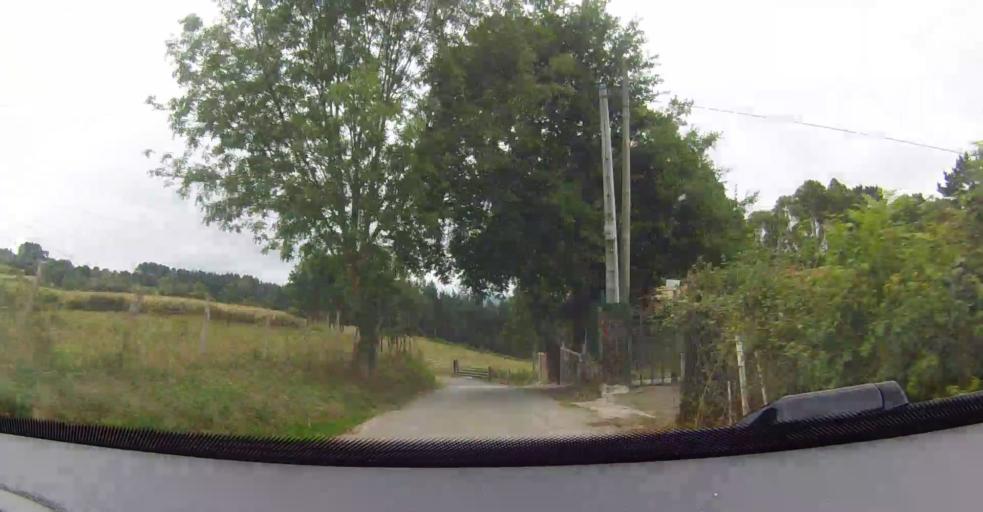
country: ES
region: Basque Country
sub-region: Bizkaia
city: Urrestieta
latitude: 43.2345
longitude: -3.1824
